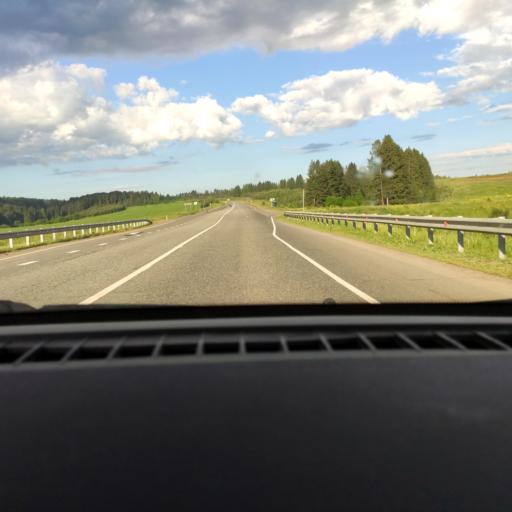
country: RU
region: Udmurtiya
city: Votkinsk
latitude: 57.2618
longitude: 54.2390
